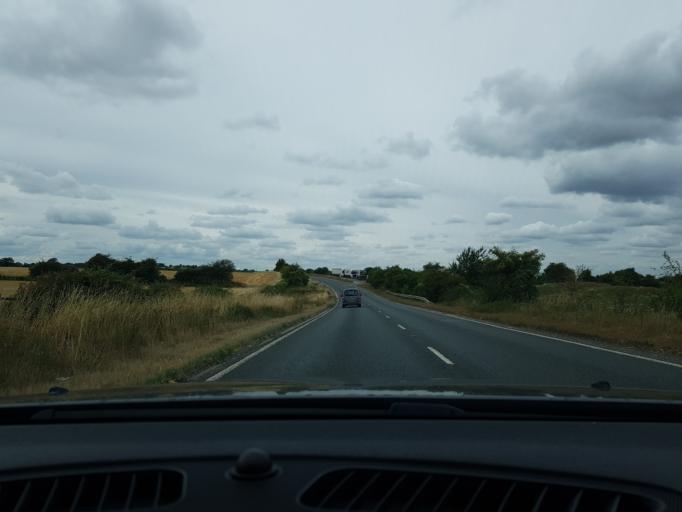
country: GB
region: England
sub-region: Hampshire
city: Basingstoke
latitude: 51.2827
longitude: -1.1317
